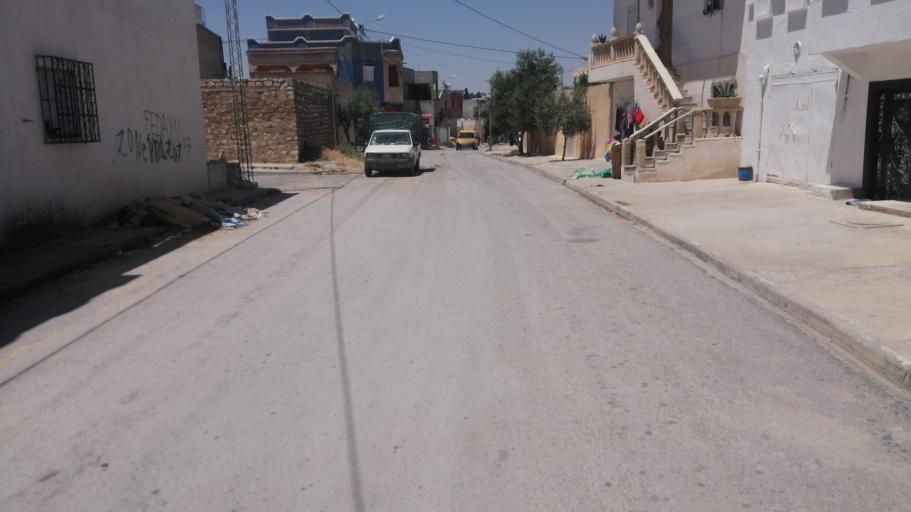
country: TN
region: Silyanah
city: Maktar
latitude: 35.8579
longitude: 9.2103
